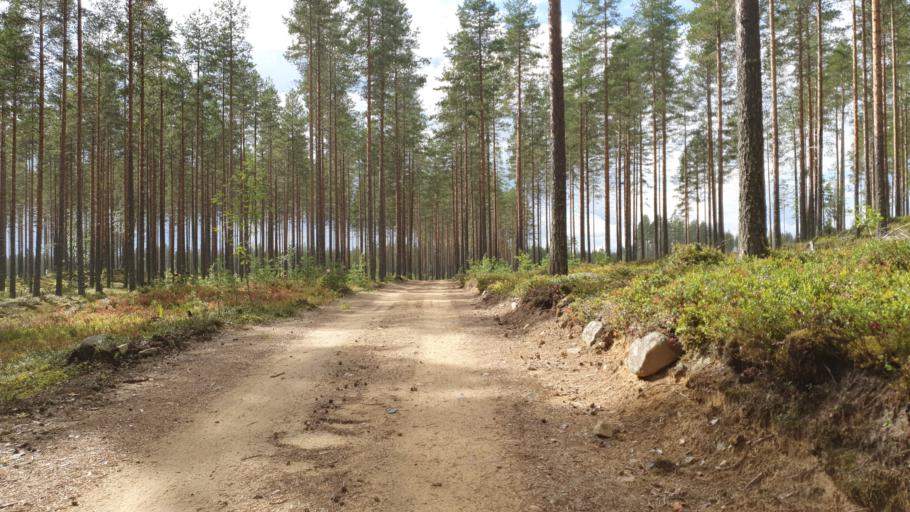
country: FI
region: Kainuu
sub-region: Kehys-Kainuu
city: Kuhmo
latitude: 64.1488
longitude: 29.3829
